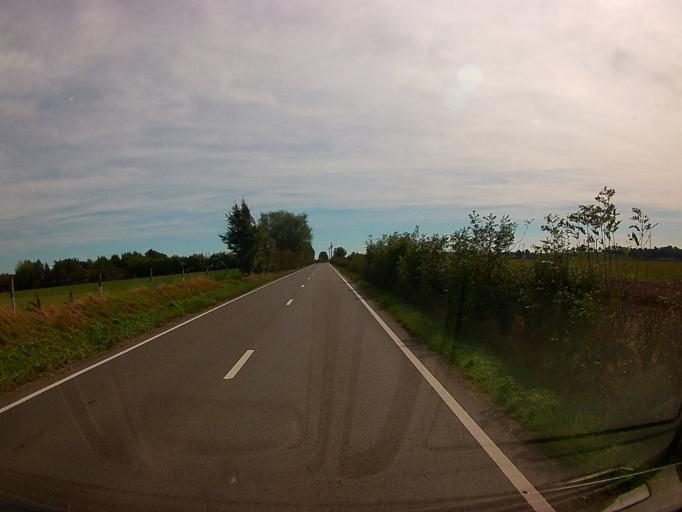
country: BE
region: Wallonia
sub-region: Province de Liege
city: Aubel
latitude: 50.6871
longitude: 5.9106
